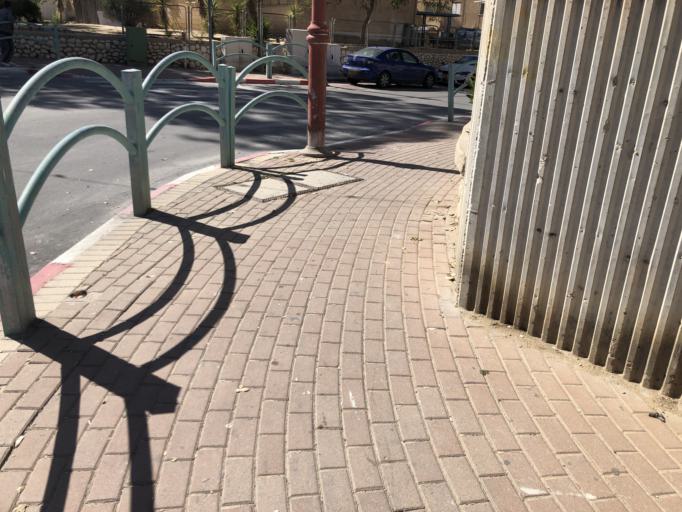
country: IL
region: Southern District
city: Dimona
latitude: 31.0653
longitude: 35.0393
